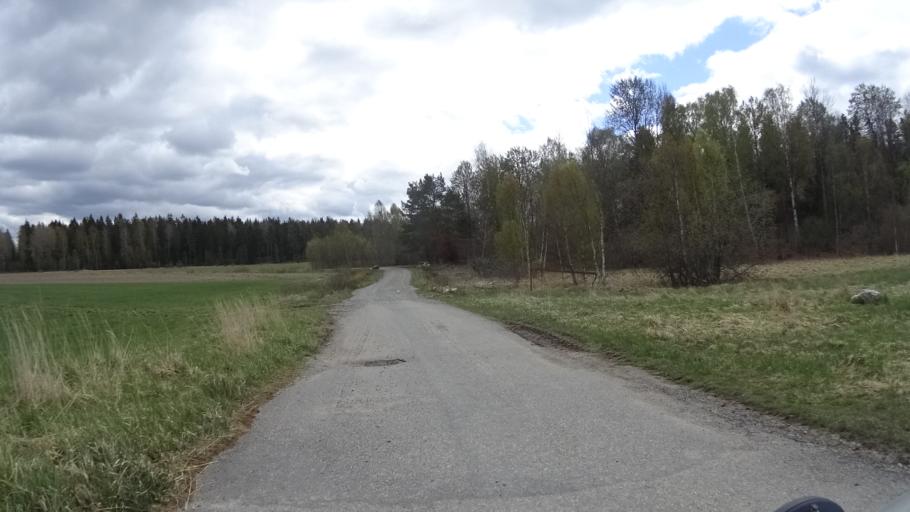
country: SE
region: Stockholm
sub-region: Botkyrka Kommun
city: Tullinge
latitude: 59.1769
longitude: 17.8993
